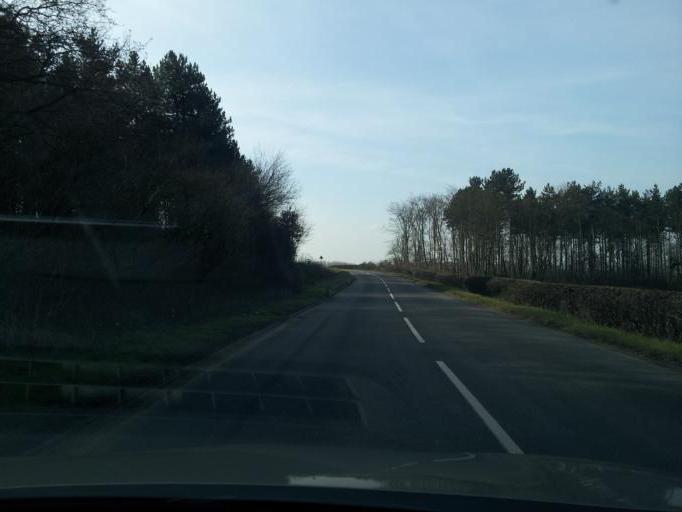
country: GB
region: England
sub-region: Nottinghamshire
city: Gotham
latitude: 52.8573
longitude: -1.2287
